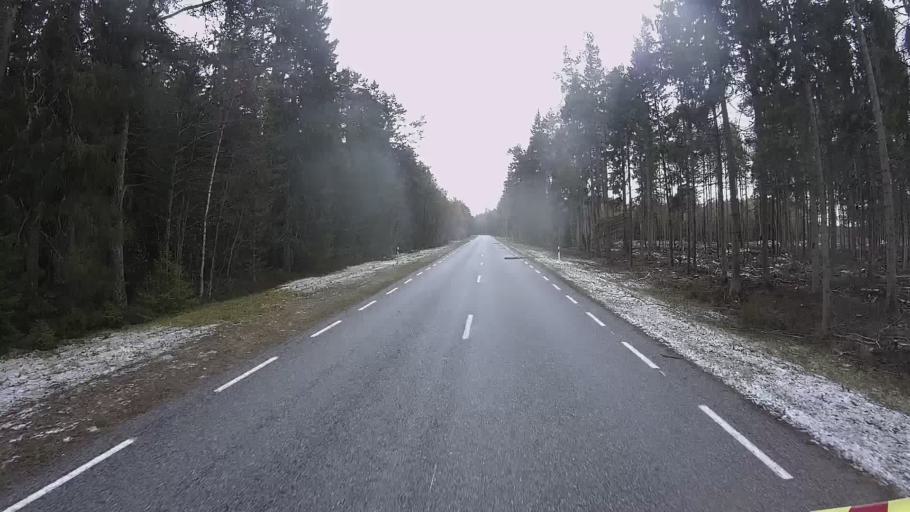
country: EE
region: Hiiumaa
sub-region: Kaerdla linn
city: Kardla
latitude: 59.0459
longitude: 22.6813
